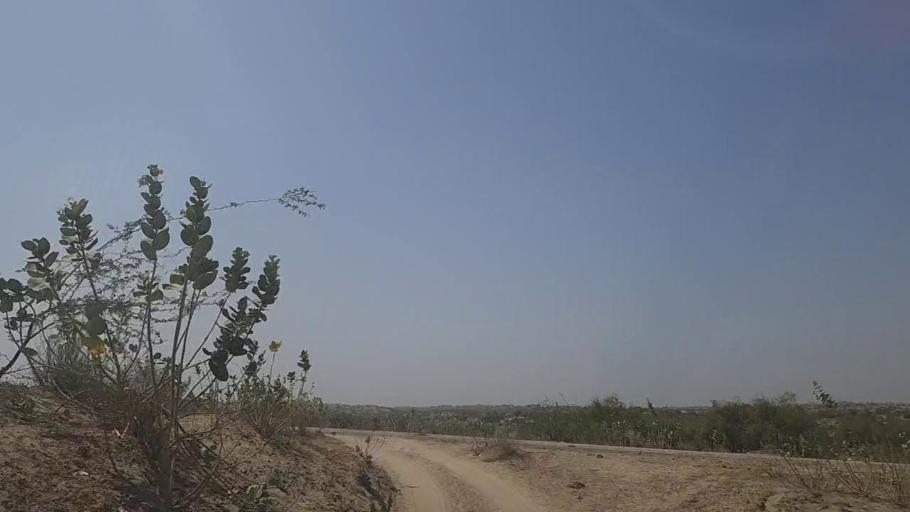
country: PK
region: Sindh
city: Naukot
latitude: 24.8196
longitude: 69.4796
